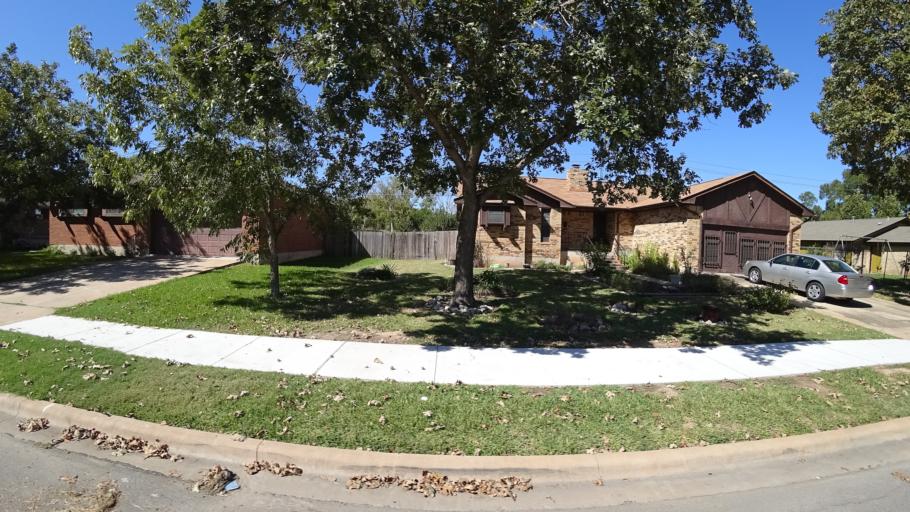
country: US
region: Texas
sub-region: Travis County
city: Hornsby Bend
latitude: 30.3061
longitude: -97.6562
